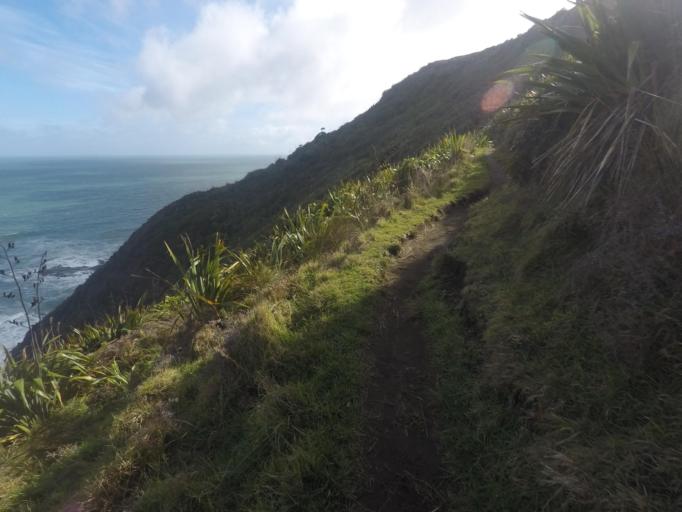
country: NZ
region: Auckland
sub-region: Auckland
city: Muriwai Beach
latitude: -36.8666
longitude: 174.4365
